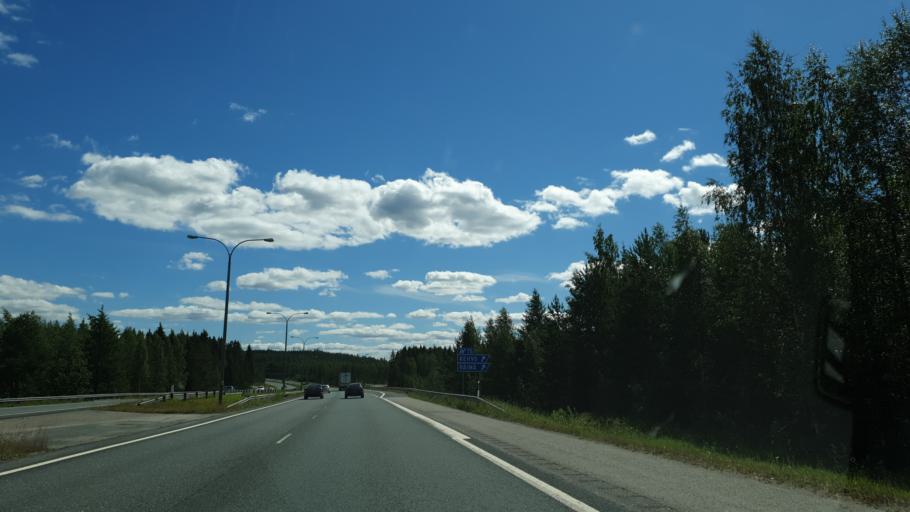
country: FI
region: Northern Savo
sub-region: Kuopio
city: Siilinjaervi
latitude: 63.0242
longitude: 27.6585
